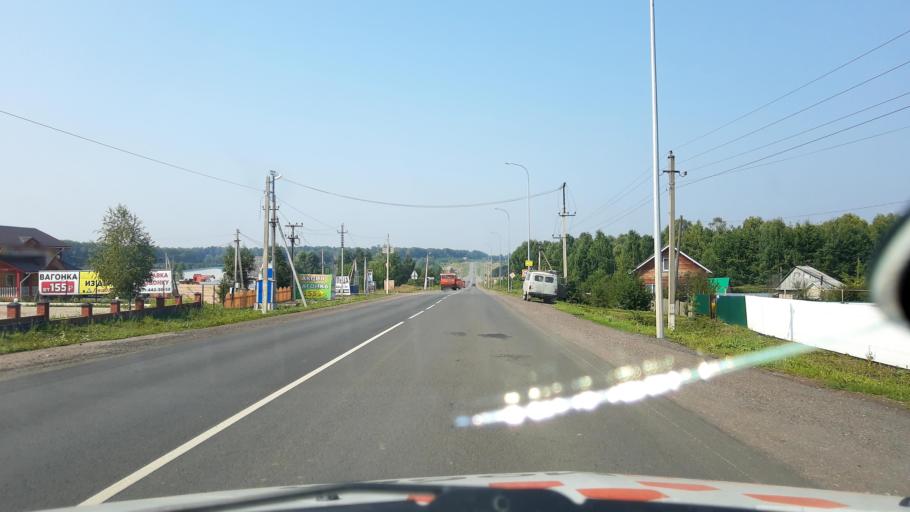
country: RU
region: Bashkortostan
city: Iglino
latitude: 54.8180
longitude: 56.3717
